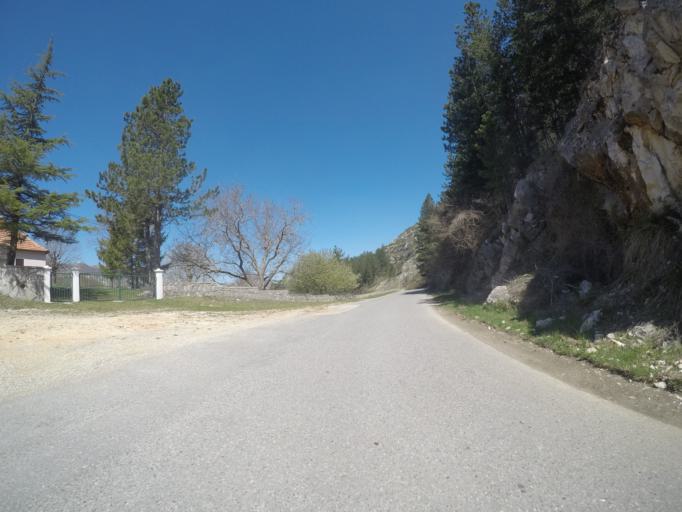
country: ME
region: Cetinje
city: Cetinje
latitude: 42.4642
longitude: 18.8613
